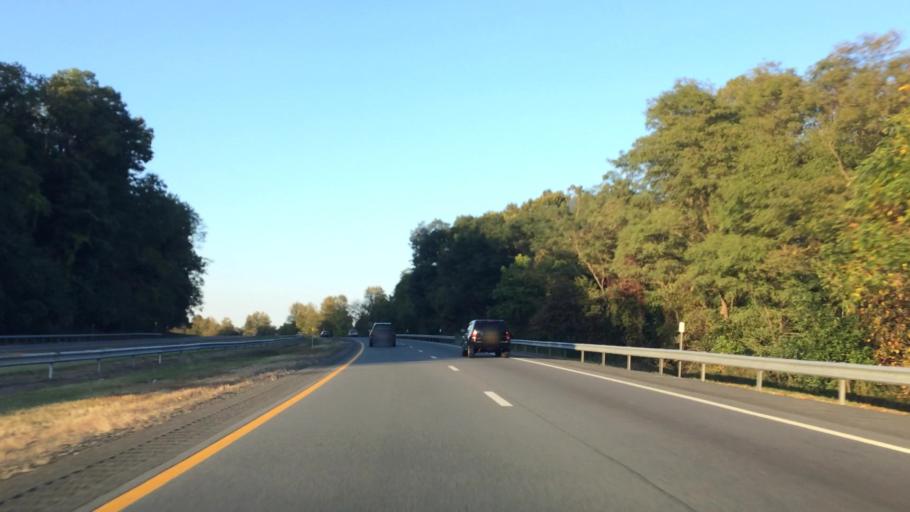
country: US
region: New York
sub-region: Orange County
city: Firthcliffe
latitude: 41.4147
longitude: -74.0710
